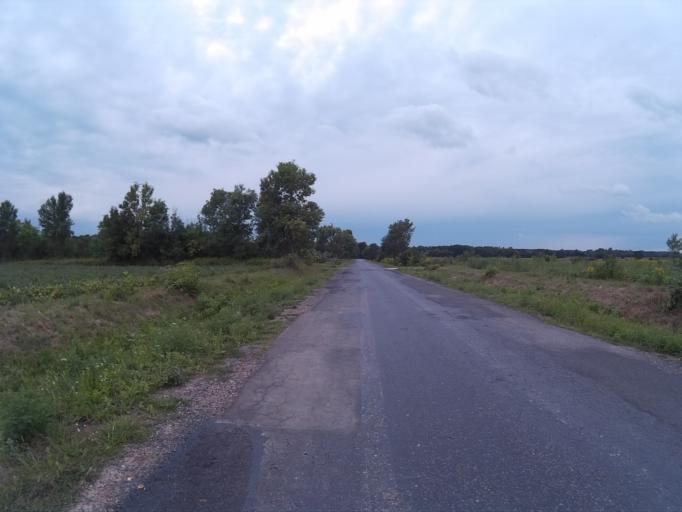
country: SI
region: Kobilje
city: Kobilje
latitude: 46.7510
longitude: 16.4886
